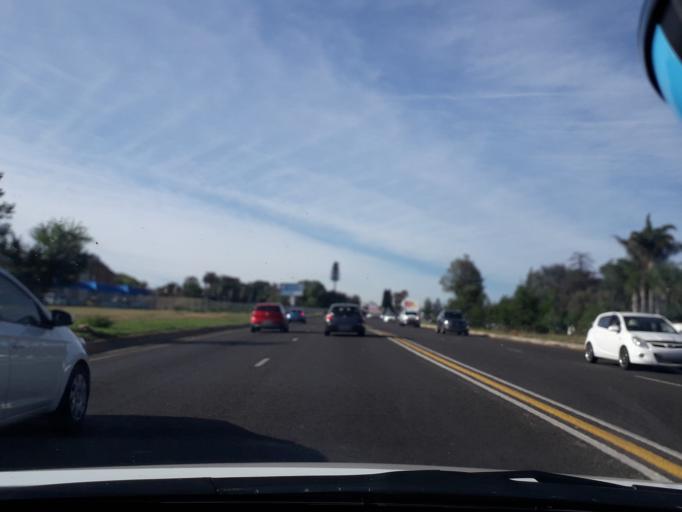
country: ZA
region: Gauteng
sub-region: City of Johannesburg Metropolitan Municipality
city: Roodepoort
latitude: -26.1001
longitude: 27.9265
